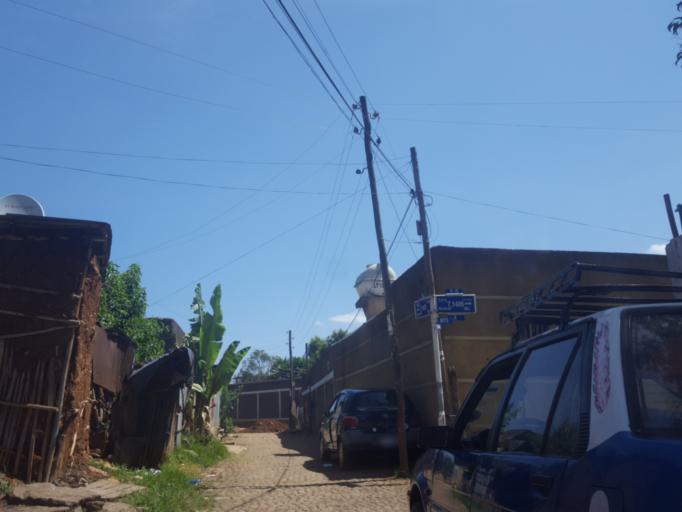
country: ET
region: Adis Abeba
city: Addis Ababa
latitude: 9.0598
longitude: 38.7394
